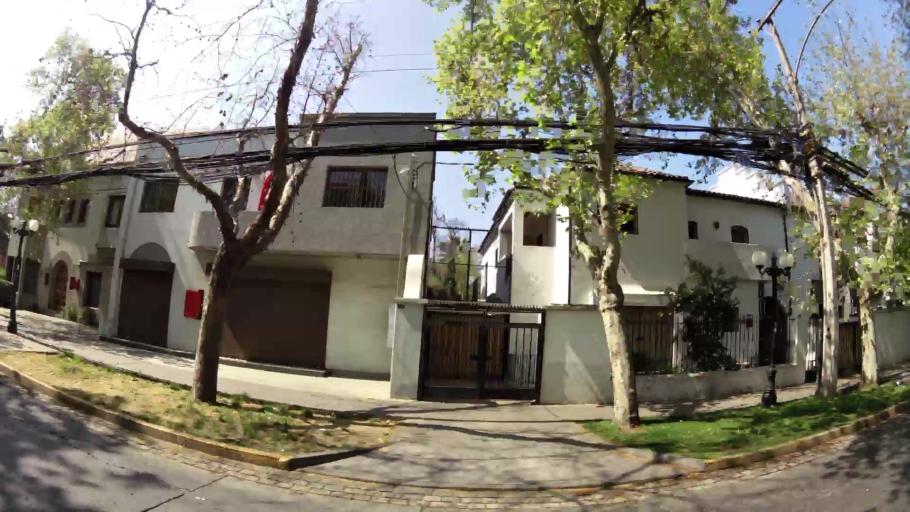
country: CL
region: Santiago Metropolitan
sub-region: Provincia de Santiago
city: Santiago
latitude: -33.4385
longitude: -70.6277
